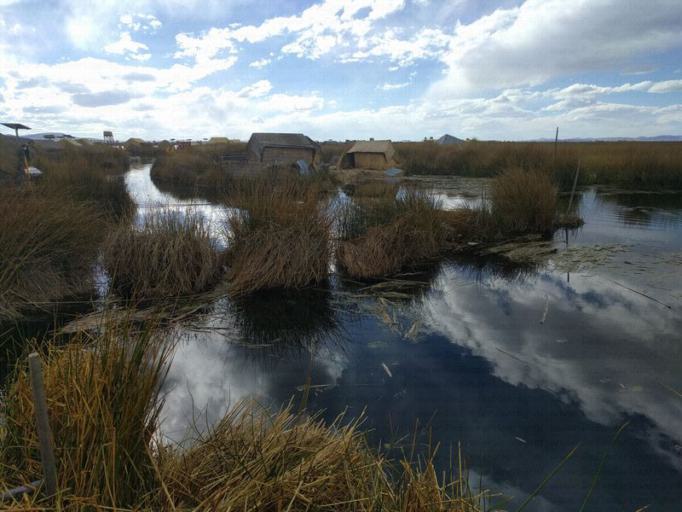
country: PE
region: Puno
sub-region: Provincia de Puno
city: Puno
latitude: -15.8161
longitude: -69.9720
